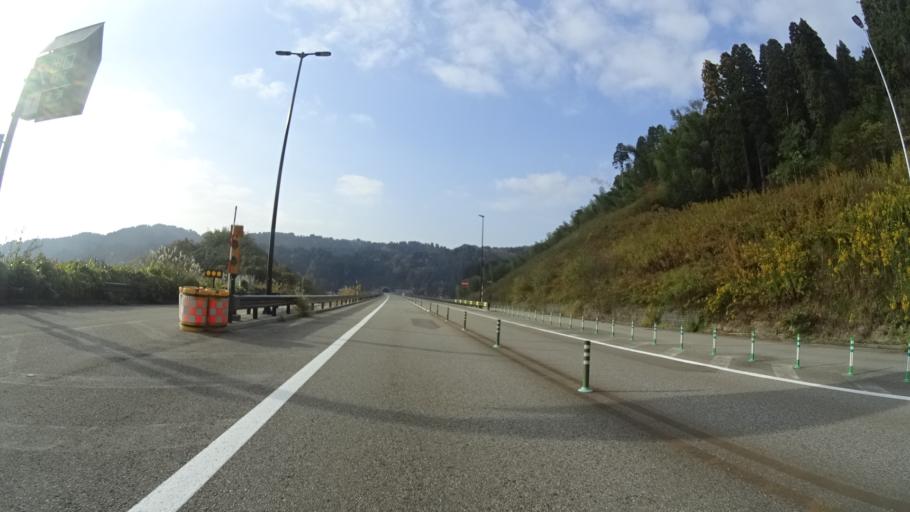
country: JP
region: Toyama
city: Himi
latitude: 36.9224
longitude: 137.0063
